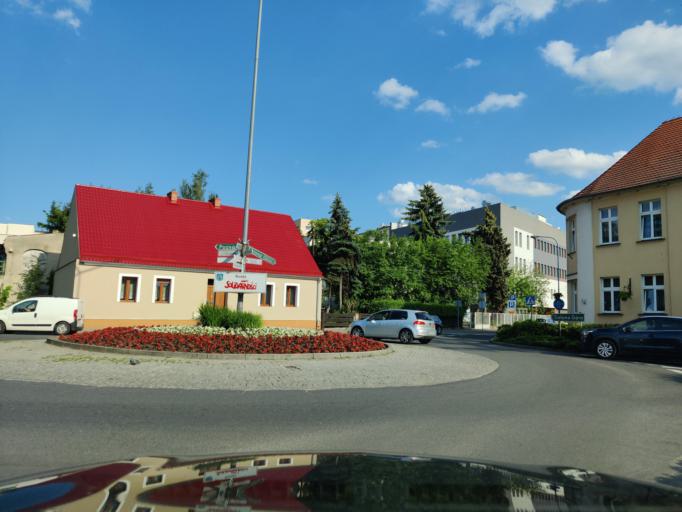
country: PL
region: Greater Poland Voivodeship
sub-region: Powiat wolsztynski
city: Wolsztyn
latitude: 52.1172
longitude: 16.1165
